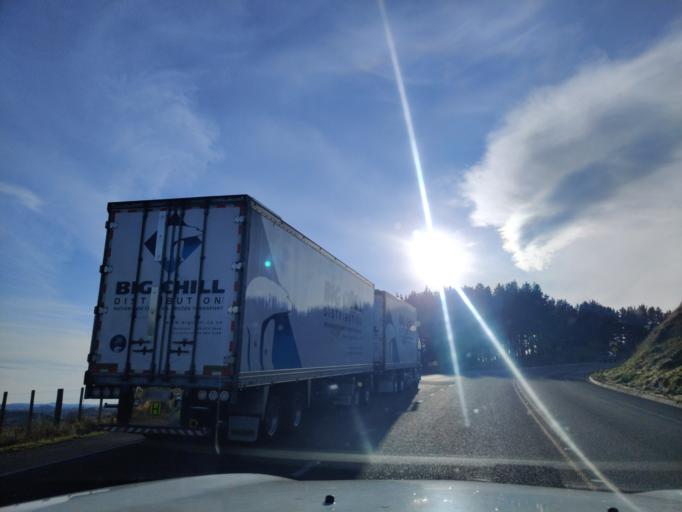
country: NZ
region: Manawatu-Wanganui
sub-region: Palmerston North City
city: Palmerston North
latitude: -40.2863
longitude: 175.7871
